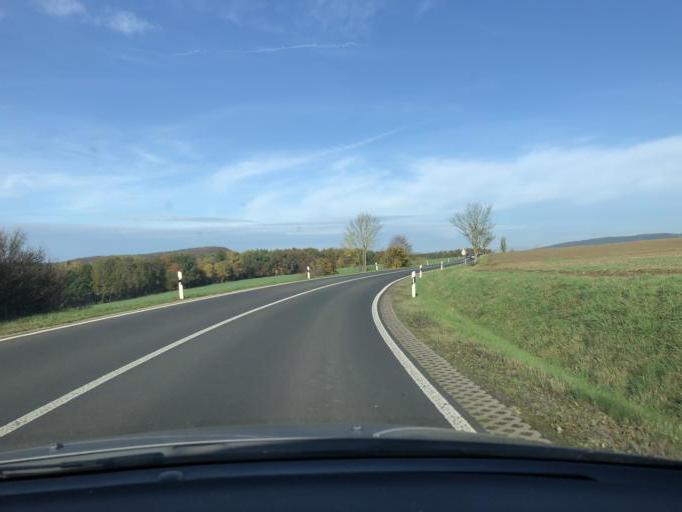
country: DE
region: Thuringia
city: Ehrenberg
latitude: 50.4703
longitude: 10.6582
